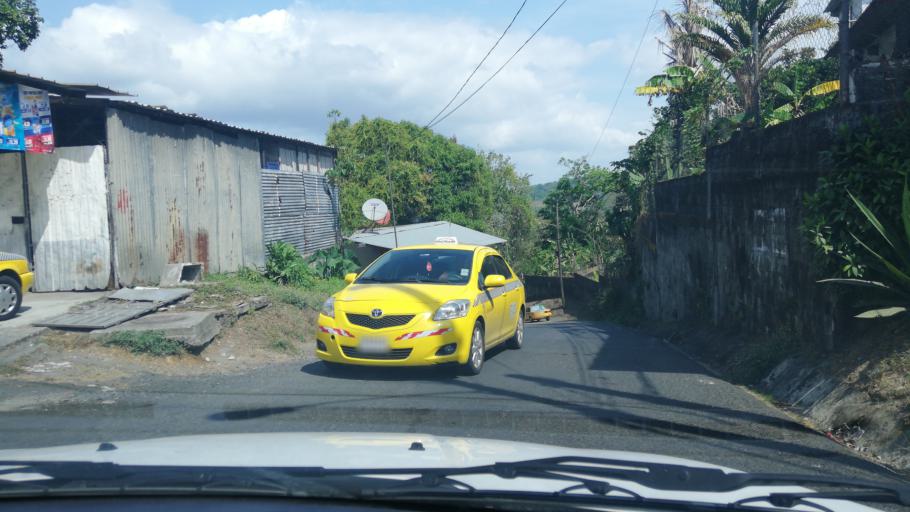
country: PA
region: Panama
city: Alcalde Diaz
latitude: 9.1211
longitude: -79.5581
